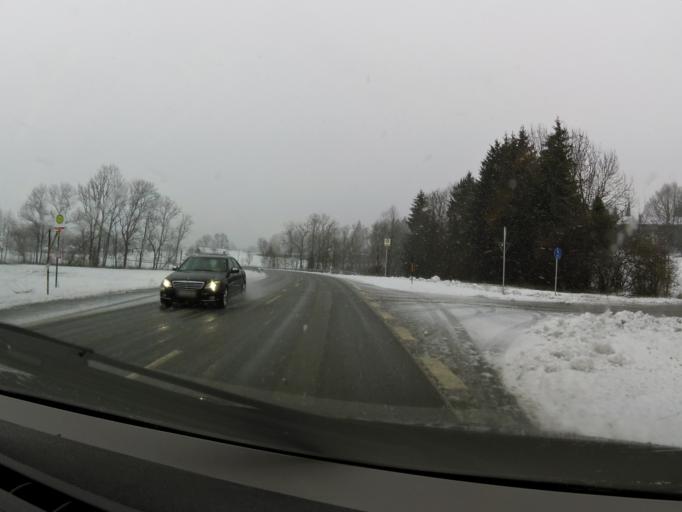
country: DE
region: Bavaria
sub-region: Upper Bavaria
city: Gmund am Tegernsee
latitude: 47.7578
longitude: 11.7050
